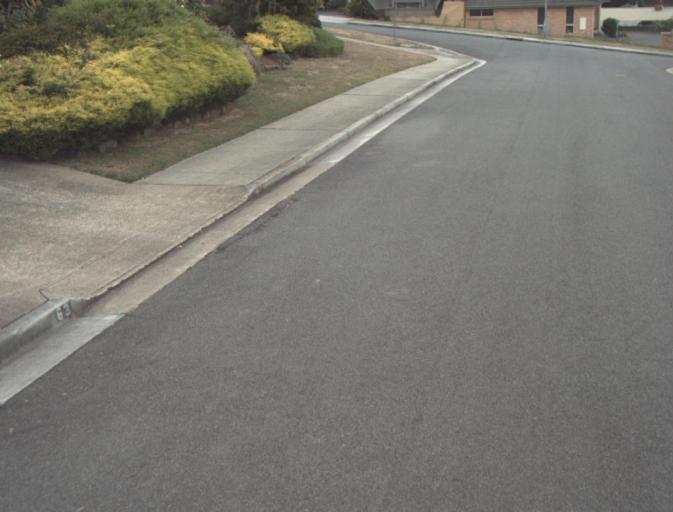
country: AU
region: Tasmania
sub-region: Launceston
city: Launceston
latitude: -41.4305
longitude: 147.1154
